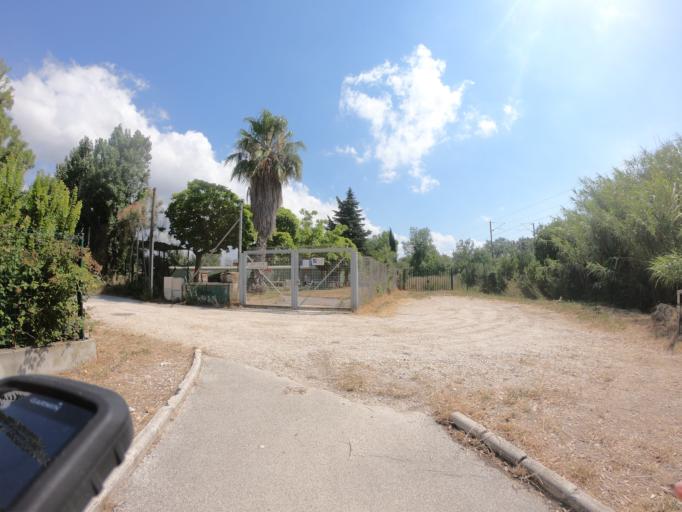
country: FR
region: Provence-Alpes-Cote d'Azur
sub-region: Departement du Var
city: La Garde
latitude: 43.1299
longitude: 6.0265
